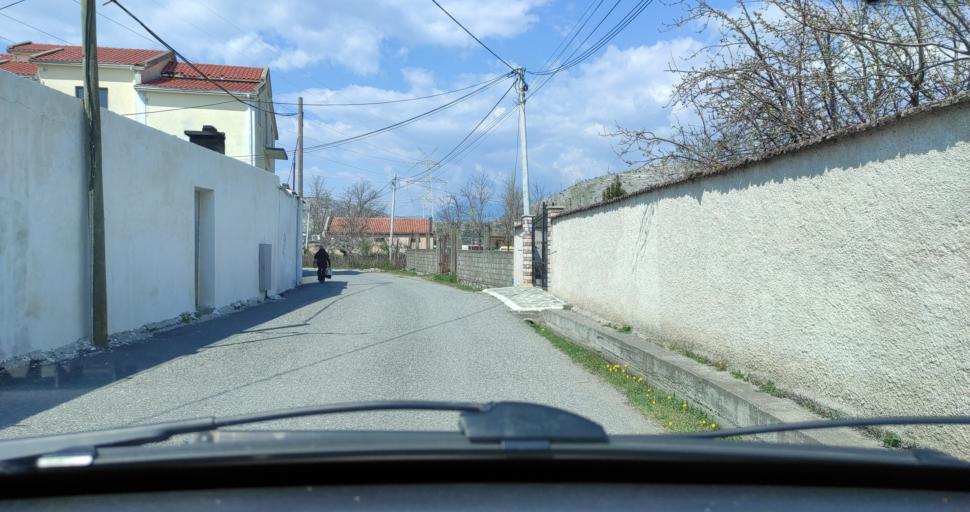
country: AL
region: Shkoder
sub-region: Rrethi i Shkodres
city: Vau i Dejes
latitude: 42.0066
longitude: 19.6419
